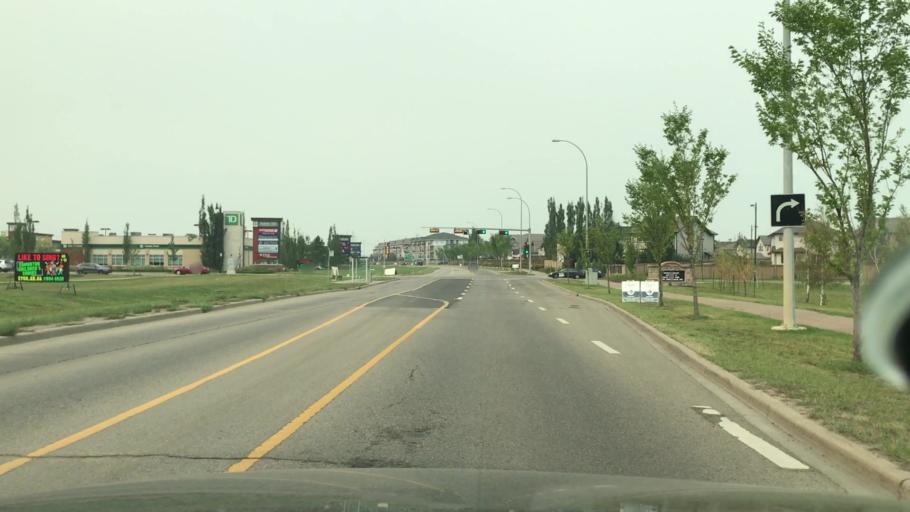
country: CA
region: Alberta
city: Edmonton
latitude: 53.4367
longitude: -113.5701
